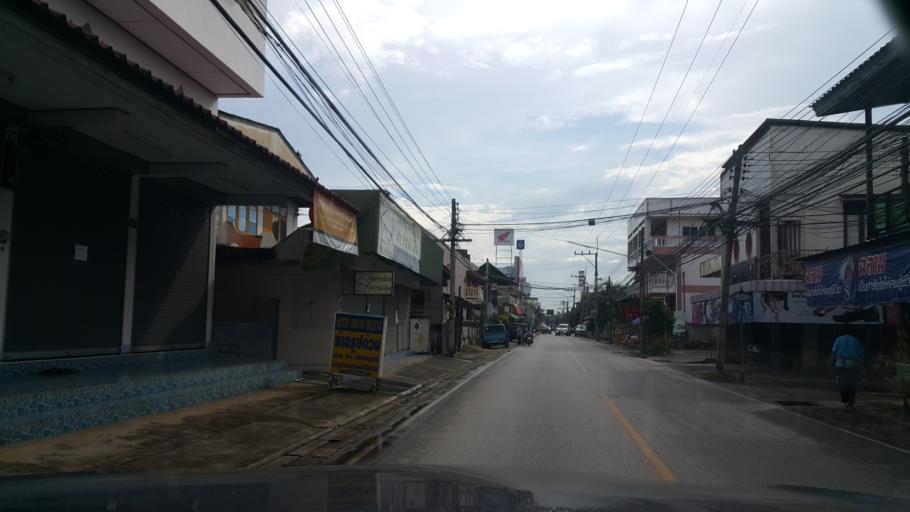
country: TH
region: Lampang
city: Thoen
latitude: 17.6086
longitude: 99.2132
